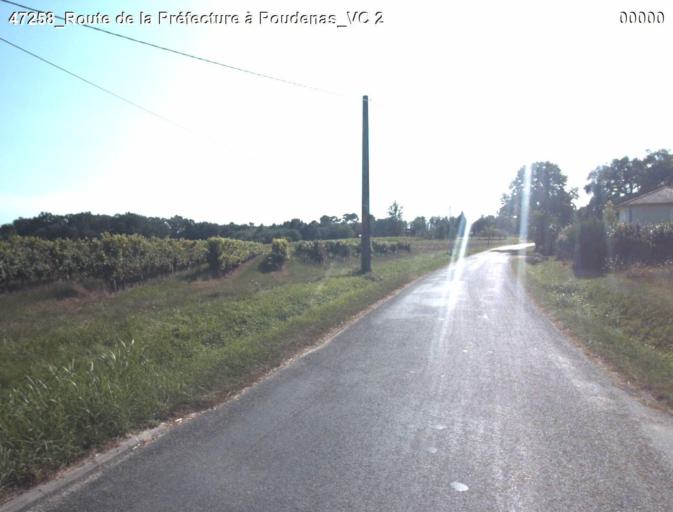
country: FR
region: Midi-Pyrenees
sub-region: Departement du Gers
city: Montreal
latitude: 44.0159
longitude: 0.1615
